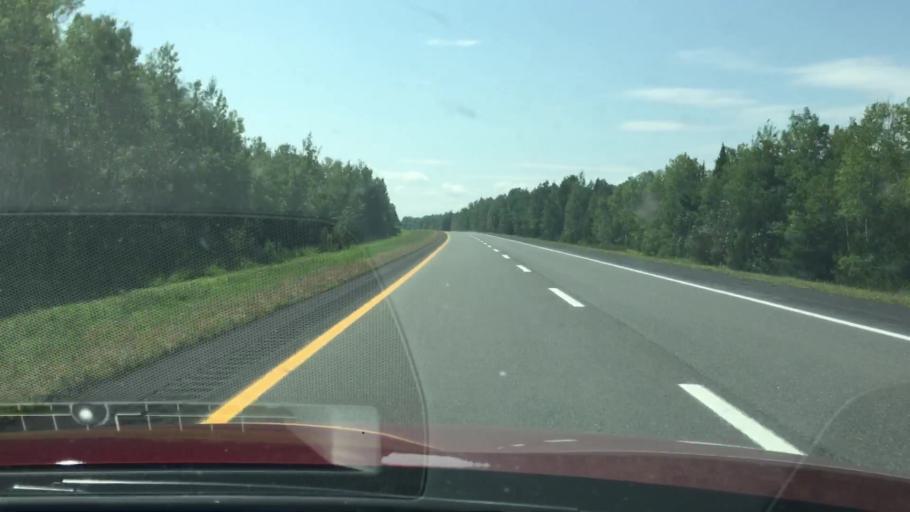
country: US
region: Maine
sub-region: Penobscot County
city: Patten
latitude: 45.9545
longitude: -68.3296
